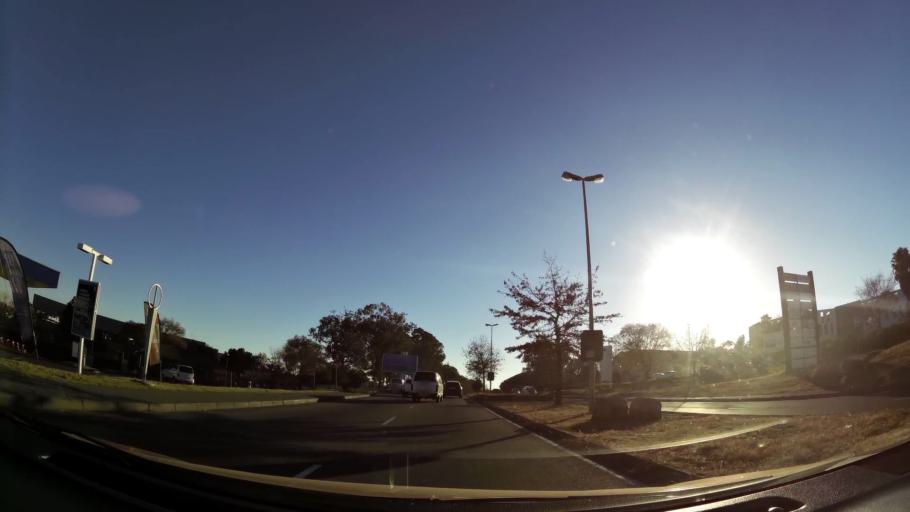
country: ZA
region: Gauteng
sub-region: City of Johannesburg Metropolitan Municipality
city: Midrand
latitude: -26.0017
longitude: 28.1248
